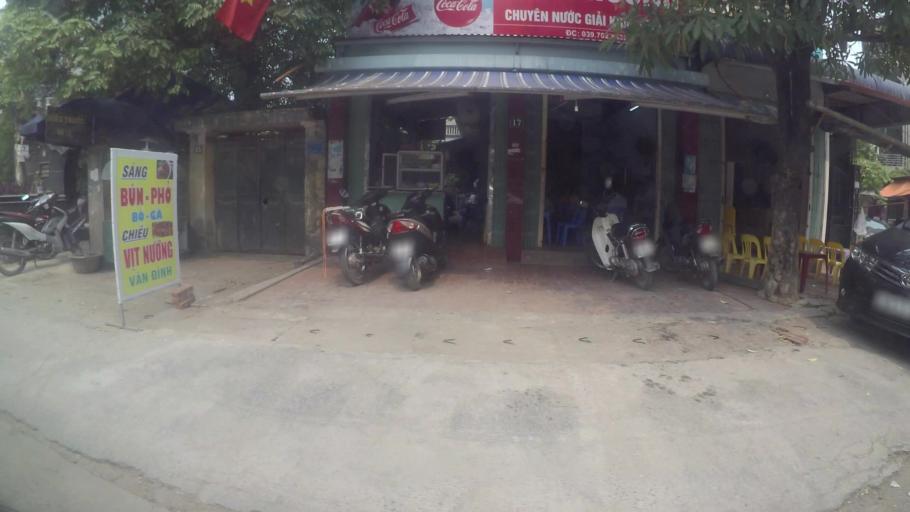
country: VN
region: Ha Noi
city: Ha Dong
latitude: 20.9675
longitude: 105.7597
